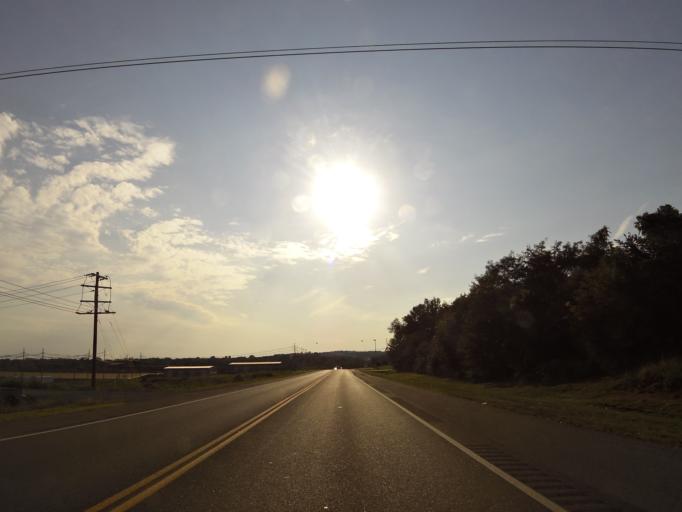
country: US
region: Tennessee
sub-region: Monroe County
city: Sweetwater
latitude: 35.6086
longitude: -84.4511
